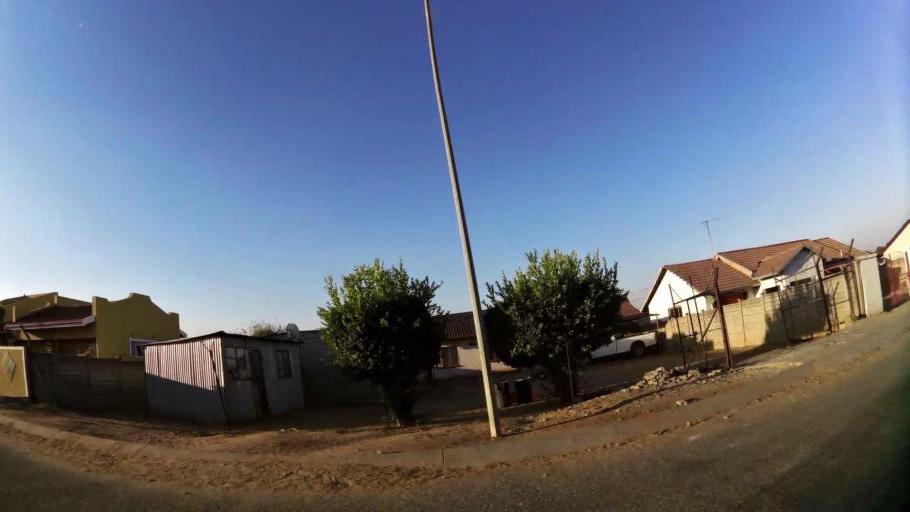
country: ZA
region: North-West
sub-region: Bojanala Platinum District Municipality
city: Rustenburg
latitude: -25.6436
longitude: 27.2088
